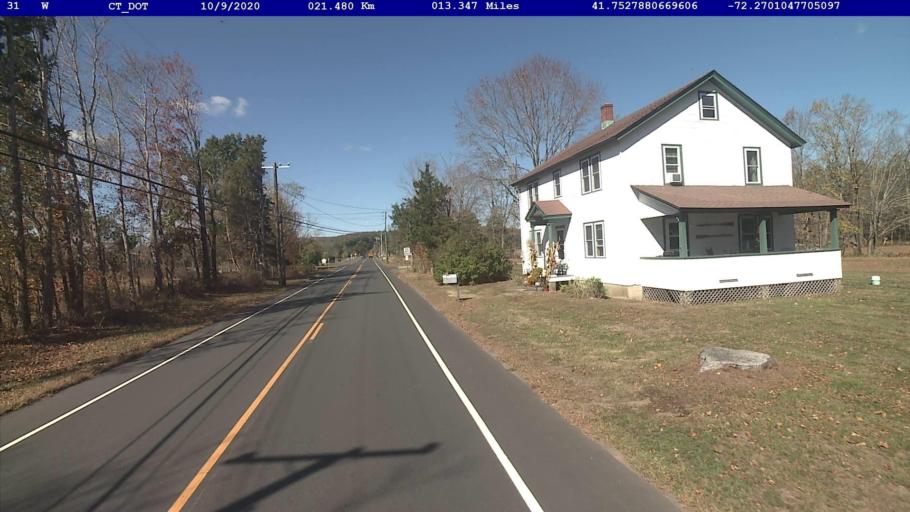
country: US
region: Connecticut
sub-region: Tolland County
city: Mansfield City
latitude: 41.7528
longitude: -72.2701
